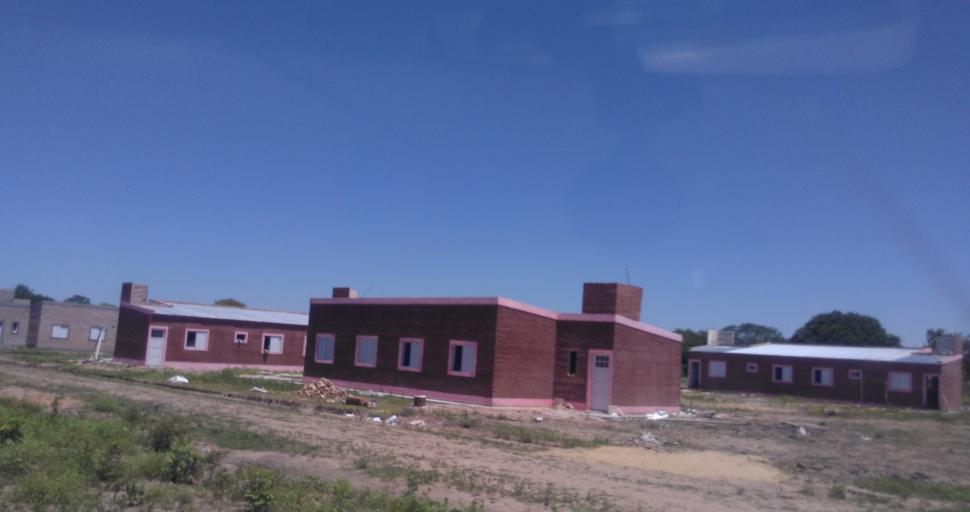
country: AR
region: Chaco
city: Fontana
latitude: -27.4116
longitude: -59.0156
